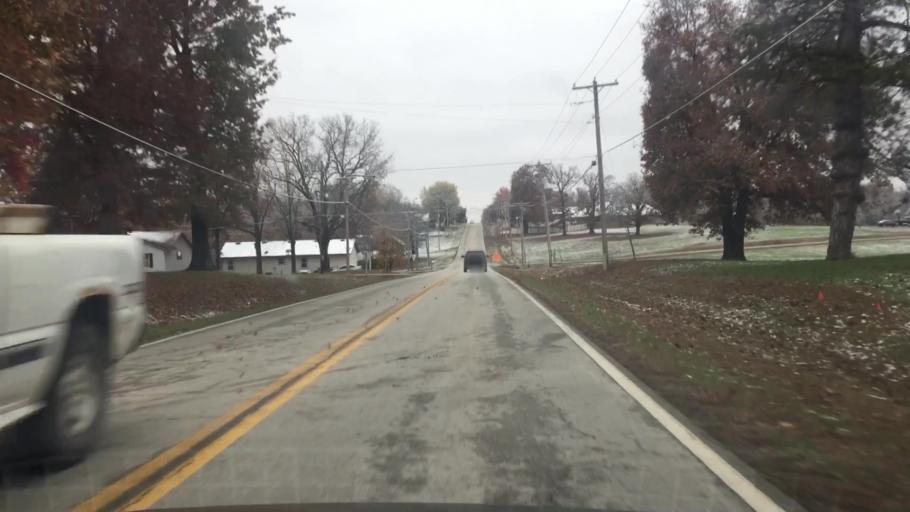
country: US
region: Missouri
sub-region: Saint Clair County
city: Osceola
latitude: 38.0317
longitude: -93.7029
